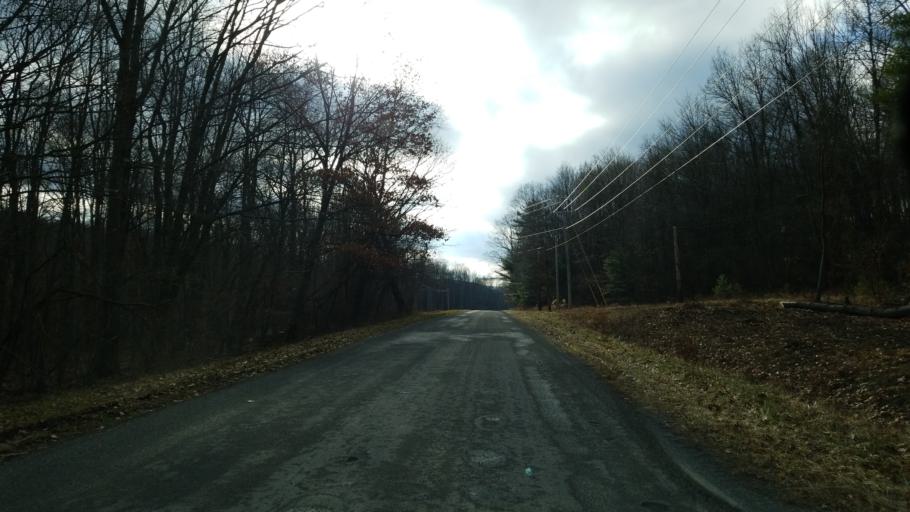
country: US
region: Pennsylvania
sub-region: Clearfield County
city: Treasure Lake
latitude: 41.1168
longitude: -78.6213
